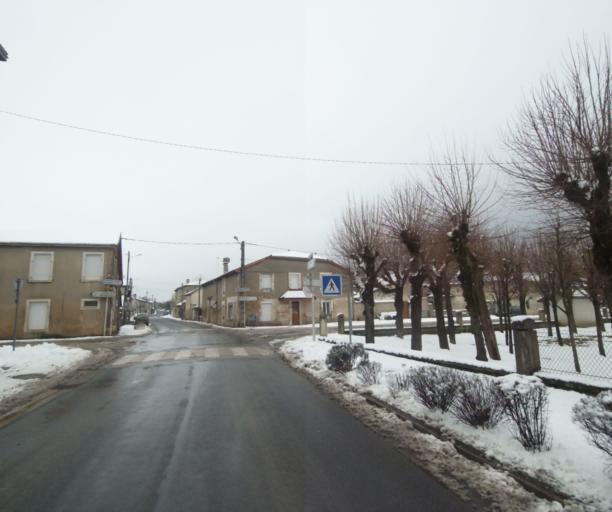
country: FR
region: Champagne-Ardenne
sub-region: Departement de la Haute-Marne
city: Wassy
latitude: 48.4718
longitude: 4.9715
